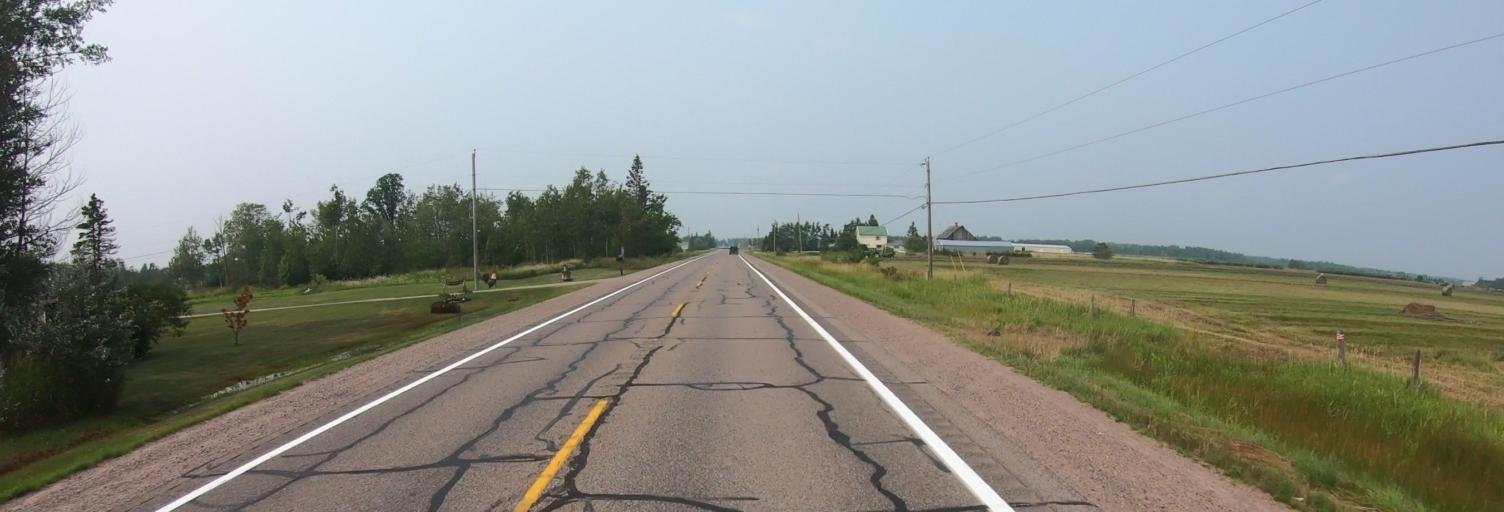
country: US
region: Michigan
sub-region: Chippewa County
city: Sault Ste. Marie
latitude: 46.4392
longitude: -84.3536
